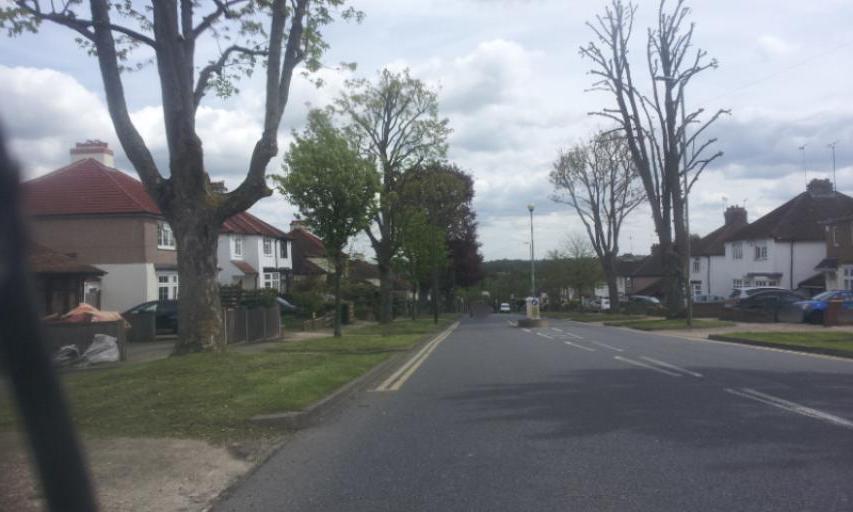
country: GB
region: England
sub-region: Greater London
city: Orpington
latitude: 51.3899
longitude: 0.1011
